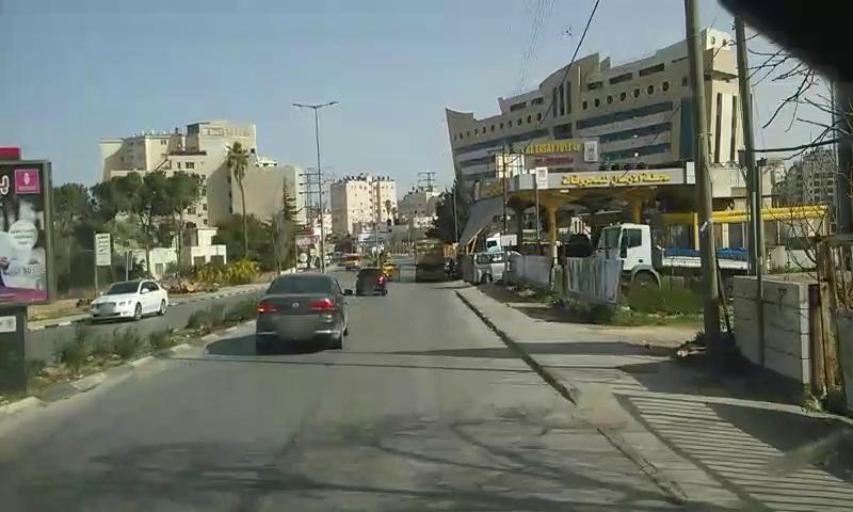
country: PS
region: West Bank
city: Surda
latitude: 31.9250
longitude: 35.2092
